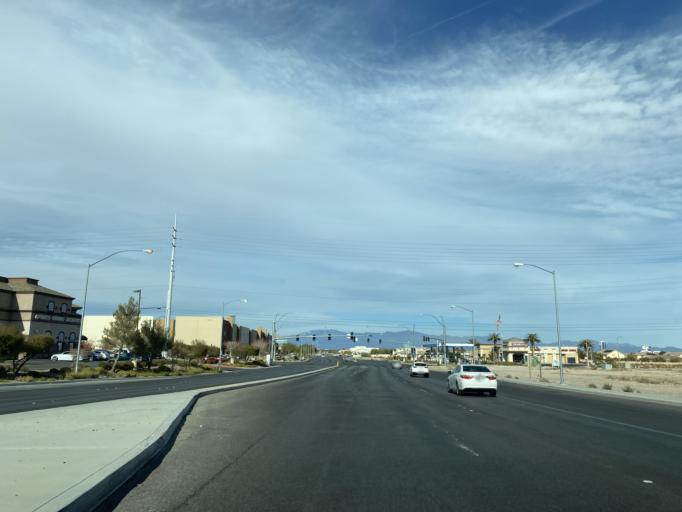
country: US
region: Nevada
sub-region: Clark County
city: Spring Valley
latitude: 36.0695
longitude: -115.2243
